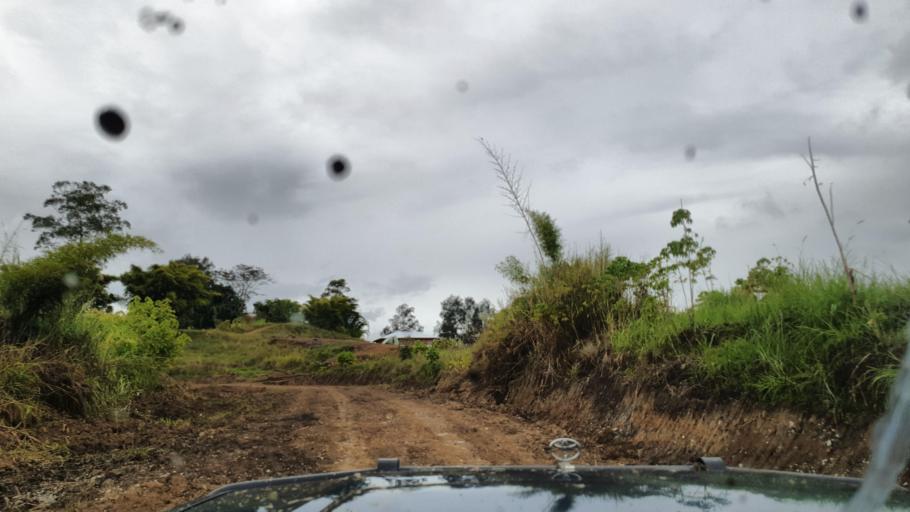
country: PG
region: Jiwaka
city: Minj
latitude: -5.9297
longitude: 144.7434
